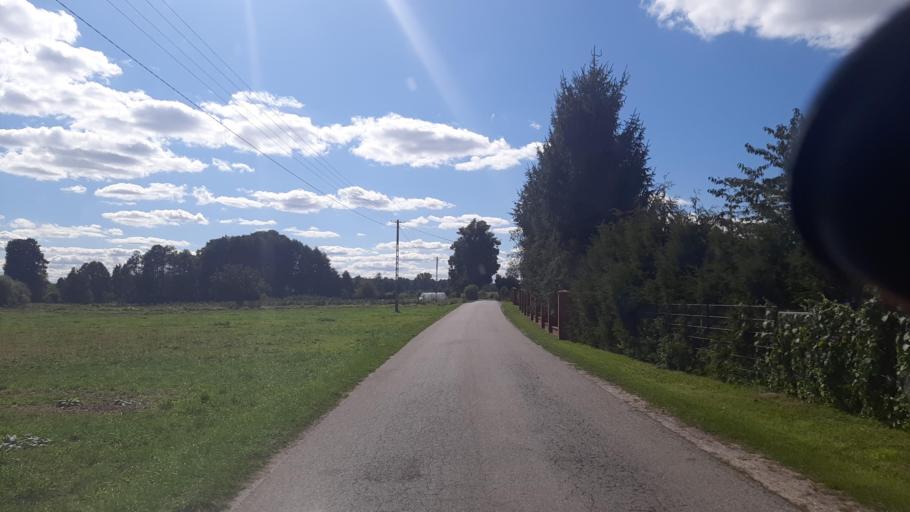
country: PL
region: Lublin Voivodeship
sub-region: Powiat lubartowski
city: Kamionka
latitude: 51.4056
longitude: 22.4135
